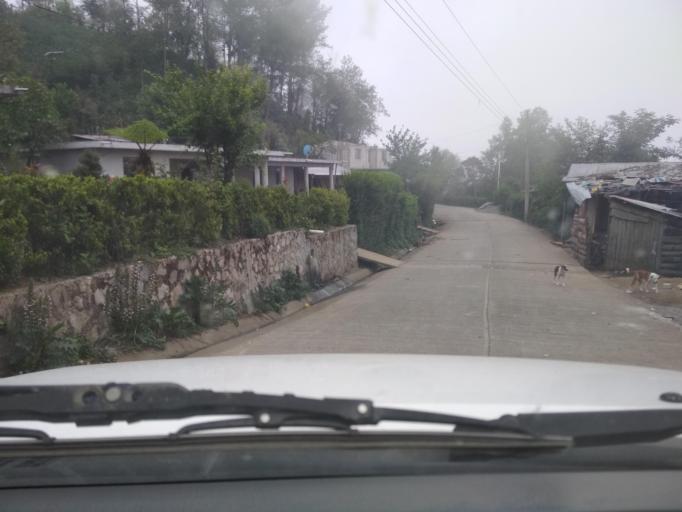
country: MX
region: Veracruz
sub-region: La Perla
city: Chilapa
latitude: 18.9968
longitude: -97.1581
